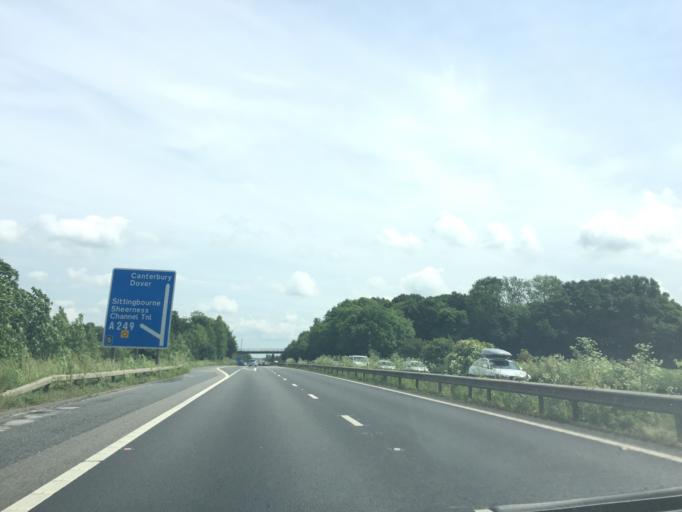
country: GB
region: England
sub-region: Kent
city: Newington
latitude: 51.3329
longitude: 0.6547
